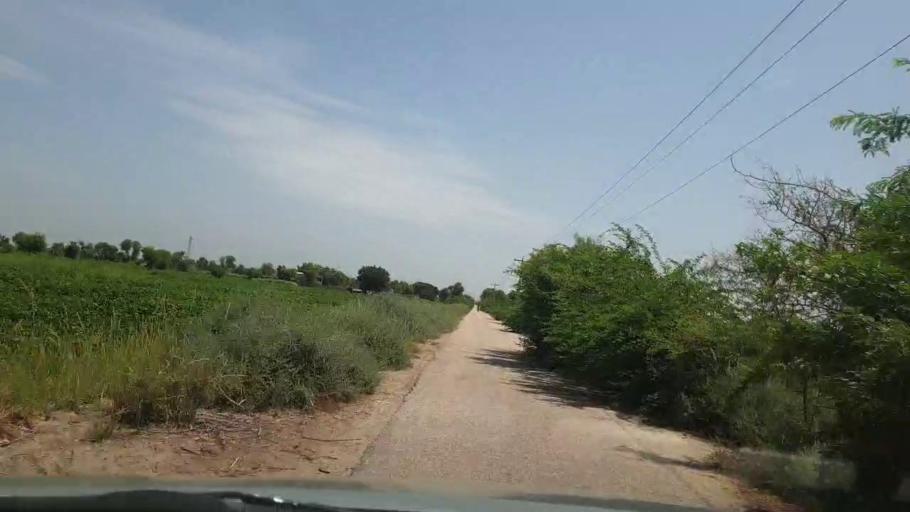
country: PK
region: Sindh
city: Bozdar
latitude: 27.1111
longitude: 68.9852
